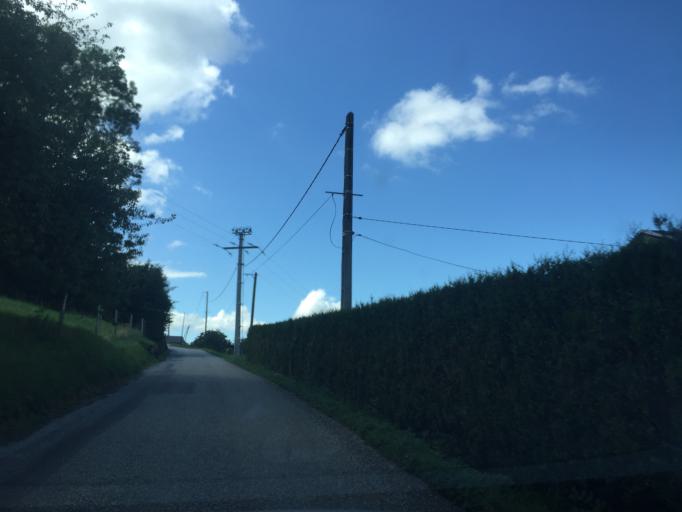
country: FR
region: Rhone-Alpes
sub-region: Departement de la Savoie
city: La Rochette
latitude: 45.4565
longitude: 6.1473
